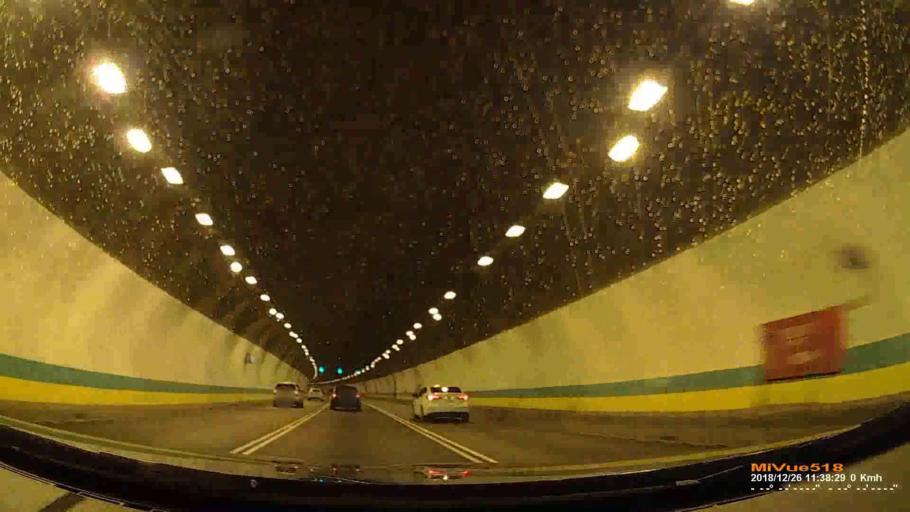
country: TW
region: Taipei
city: Taipei
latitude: 24.9807
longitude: 121.5848
